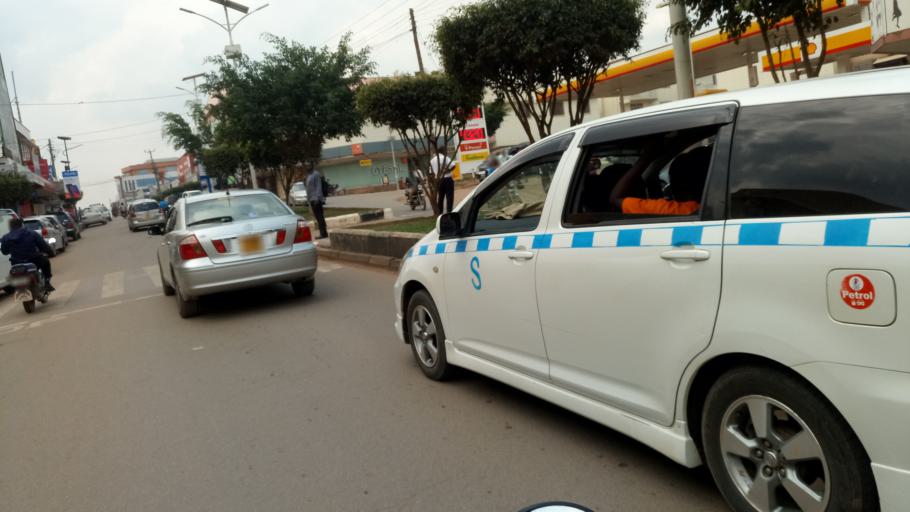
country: UG
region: Western Region
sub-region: Mbarara District
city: Mbarara
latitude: -0.6075
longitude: 30.6611
